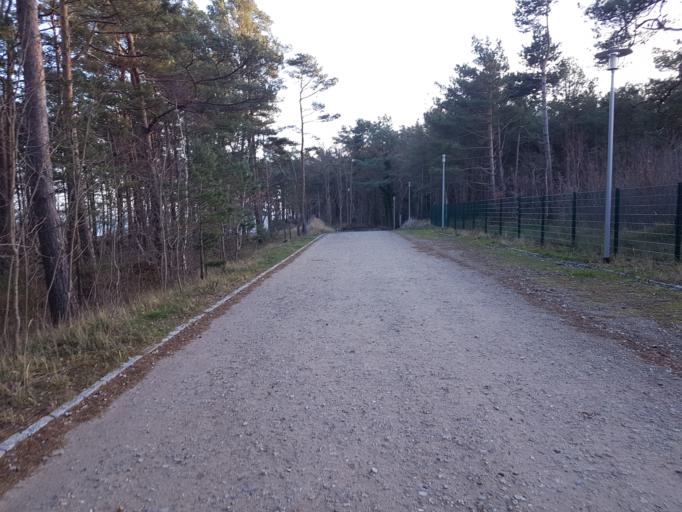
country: DE
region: Mecklenburg-Vorpommern
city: Ostseebad Binz
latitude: 54.4275
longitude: 13.5850
